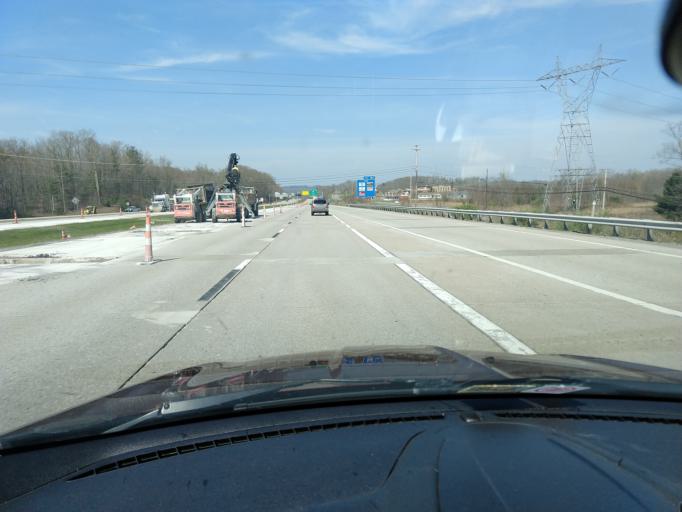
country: US
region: West Virginia
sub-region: Raleigh County
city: Daniels
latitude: 37.7668
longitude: -81.1269
